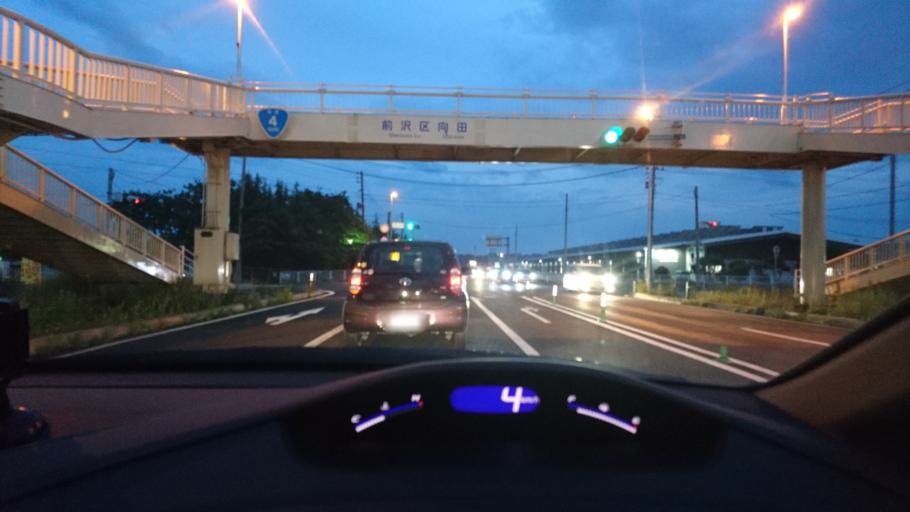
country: JP
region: Iwate
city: Mizusawa
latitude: 39.0466
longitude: 141.1303
